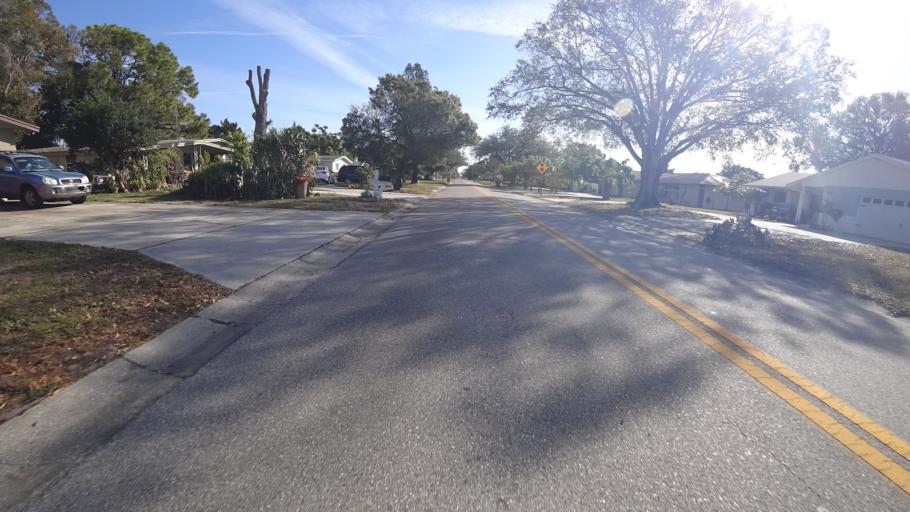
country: US
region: Florida
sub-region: Manatee County
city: West Bradenton
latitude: 27.4848
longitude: -82.6010
